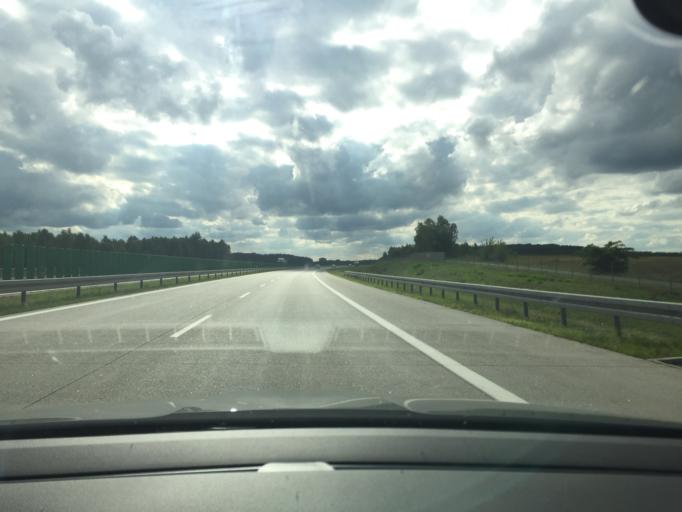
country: PL
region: Lubusz
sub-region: Powiat sulecinski
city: Torzym
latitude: 52.3328
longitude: 14.9881
